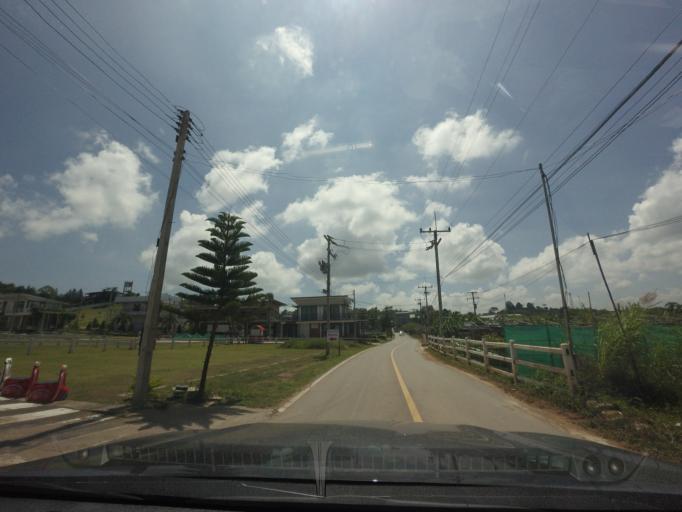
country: TH
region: Phetchabun
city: Khao Kho
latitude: 16.7733
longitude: 101.0475
